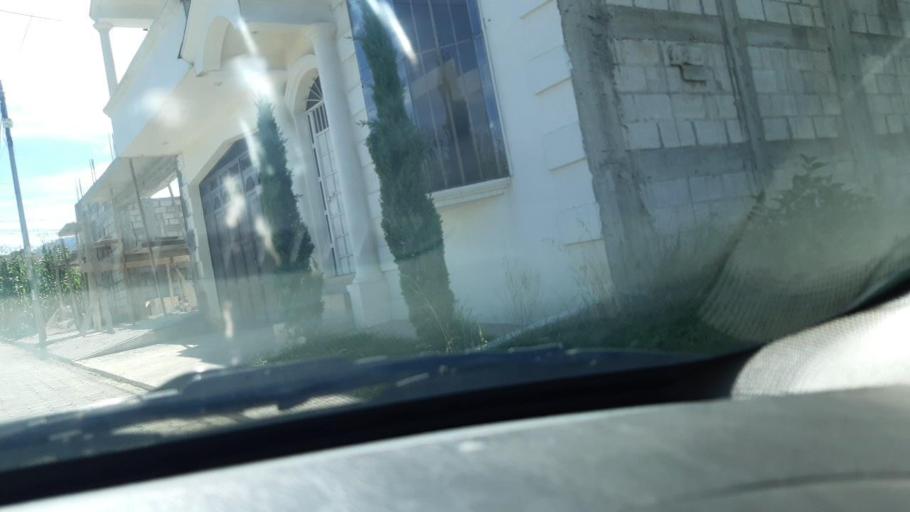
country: GT
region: Quetzaltenango
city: Salcaja
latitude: 14.8852
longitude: -91.4511
